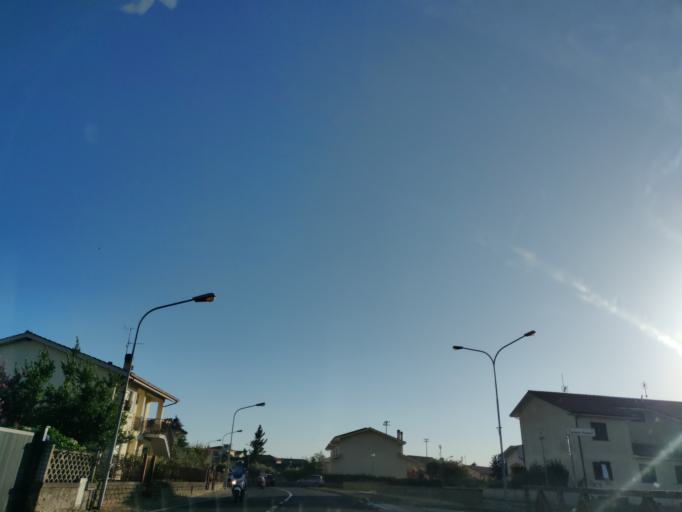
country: IT
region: Latium
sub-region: Provincia di Viterbo
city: Grotte di Castro
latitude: 42.6777
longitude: 11.8684
